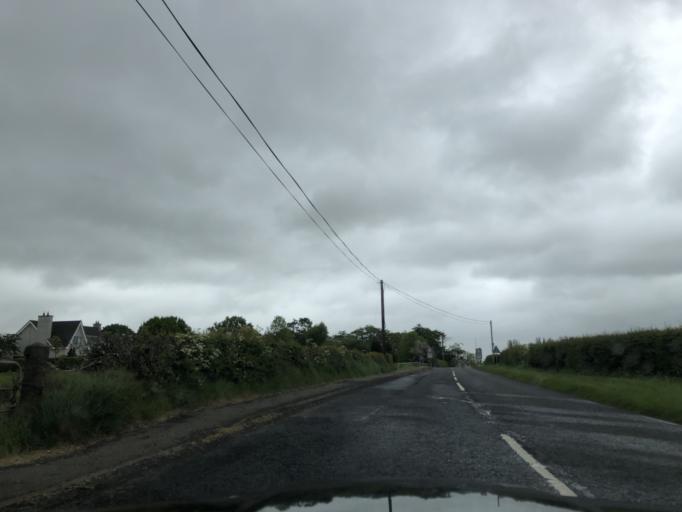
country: GB
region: Northern Ireland
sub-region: Ballymoney District
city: Ballymoney
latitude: 55.1226
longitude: -6.4823
